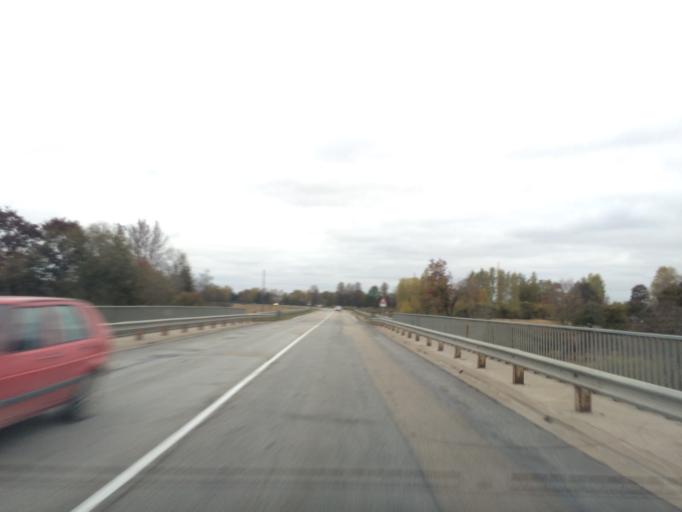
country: LV
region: Plavinu
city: Plavinas
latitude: 56.6080
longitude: 25.7834
